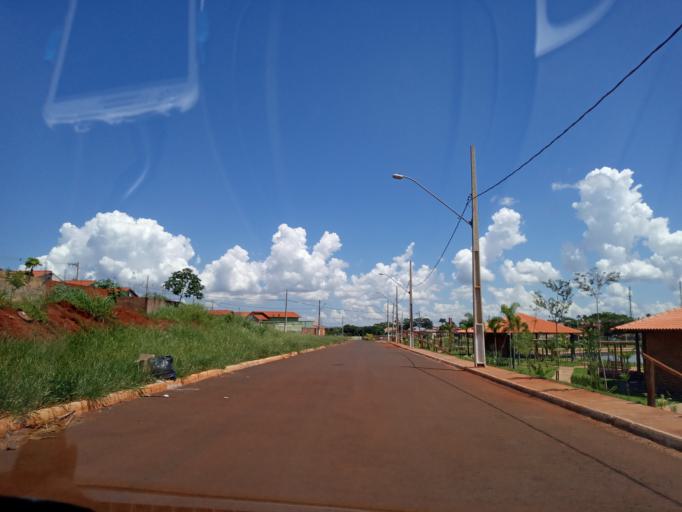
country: BR
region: Goias
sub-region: Itumbiara
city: Itumbiara
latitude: -18.4347
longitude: -49.1799
